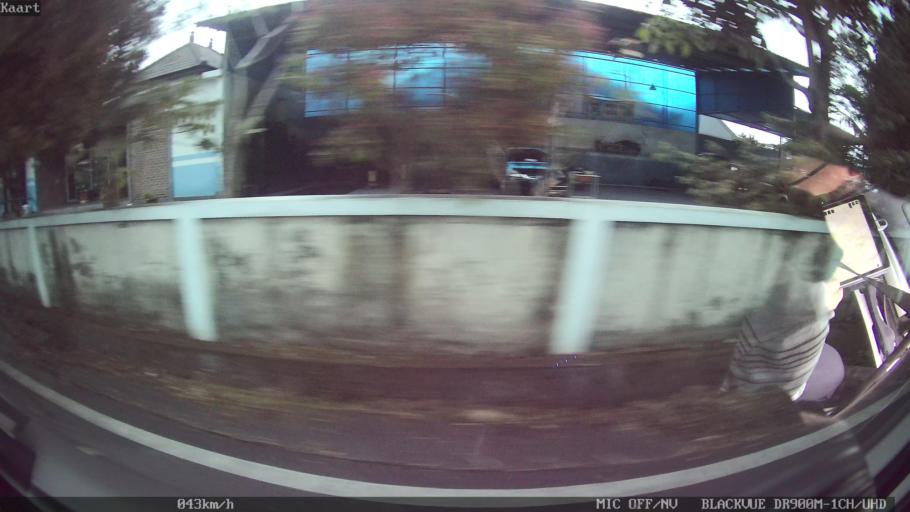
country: ID
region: Bali
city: Banjar Mambalkajanan
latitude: -8.5477
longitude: 115.2213
